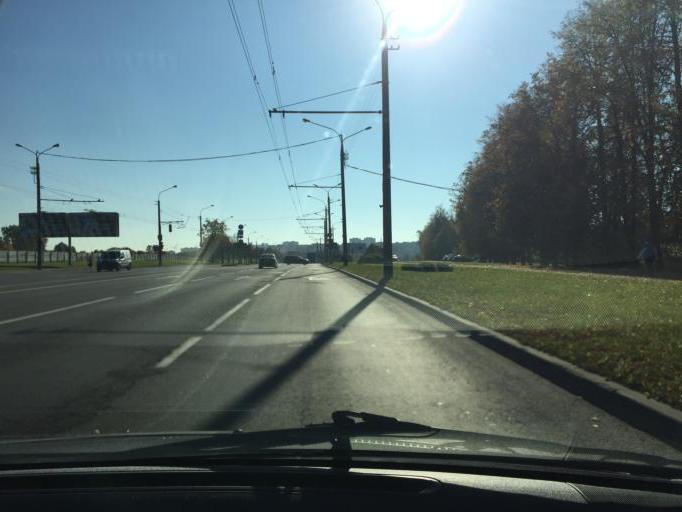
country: BY
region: Minsk
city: Syenitsa
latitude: 53.8630
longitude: 27.5330
